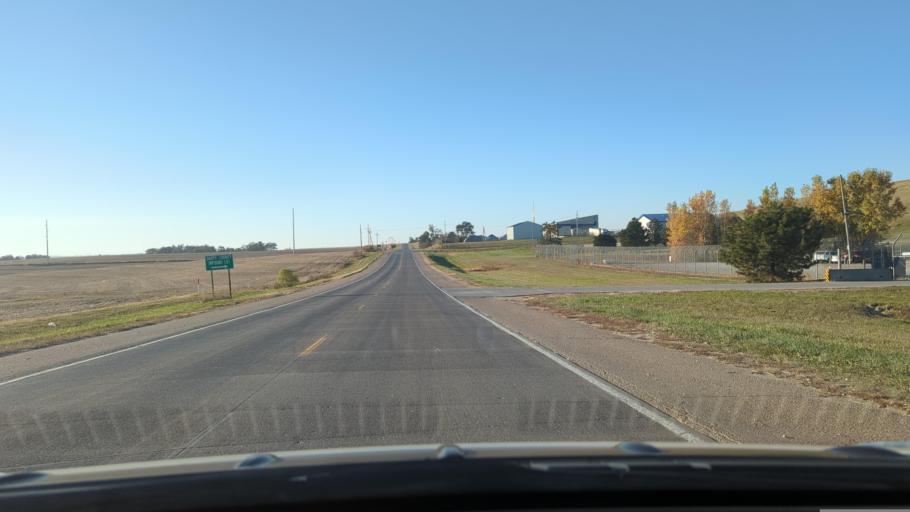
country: US
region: Nebraska
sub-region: Sarpy County
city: Springfield
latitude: 41.1017
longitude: -96.1577
